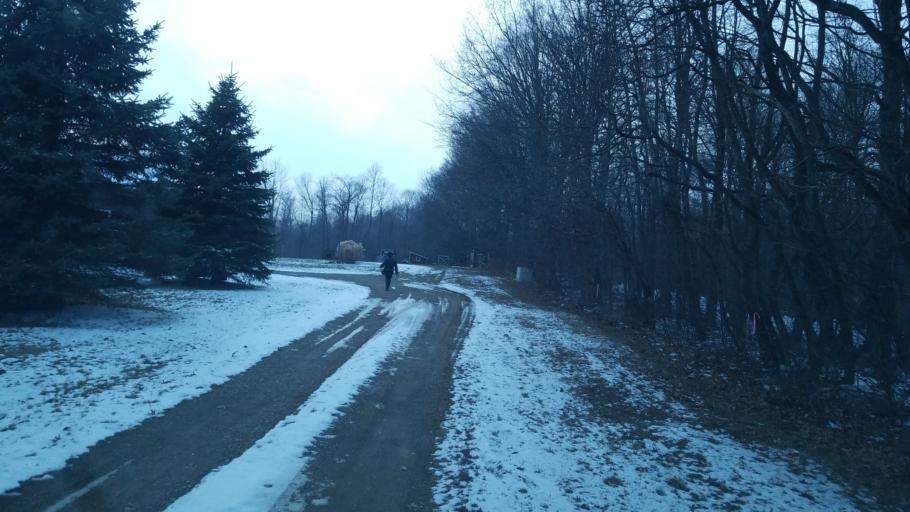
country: US
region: Ohio
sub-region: Sandusky County
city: Bellville
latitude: 40.5905
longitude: -82.5558
